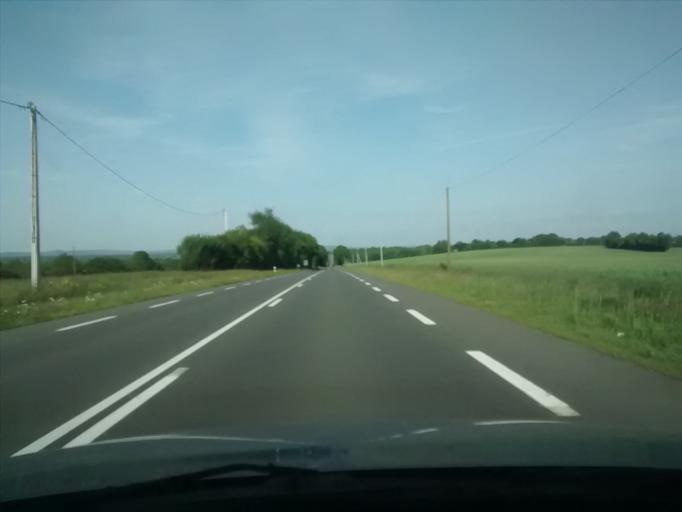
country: FR
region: Pays de la Loire
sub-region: Departement de la Mayenne
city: Vaiges
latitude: 48.0373
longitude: -0.4564
